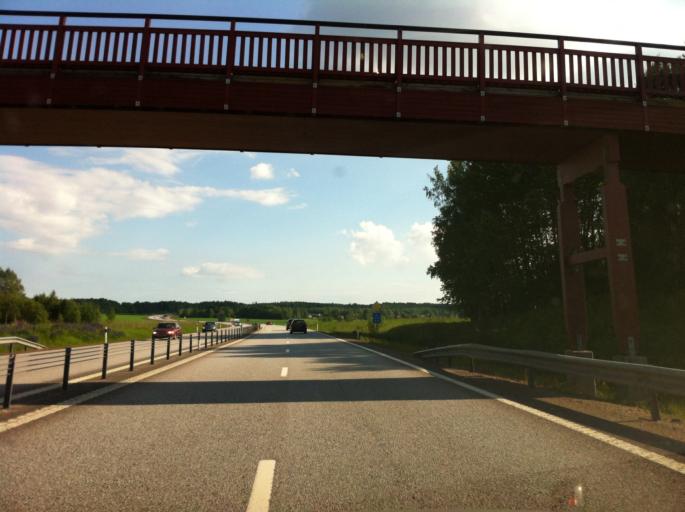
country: SE
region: Vaermland
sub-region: Karlstads Kommun
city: Karlstad
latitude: 59.4295
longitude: 13.4079
